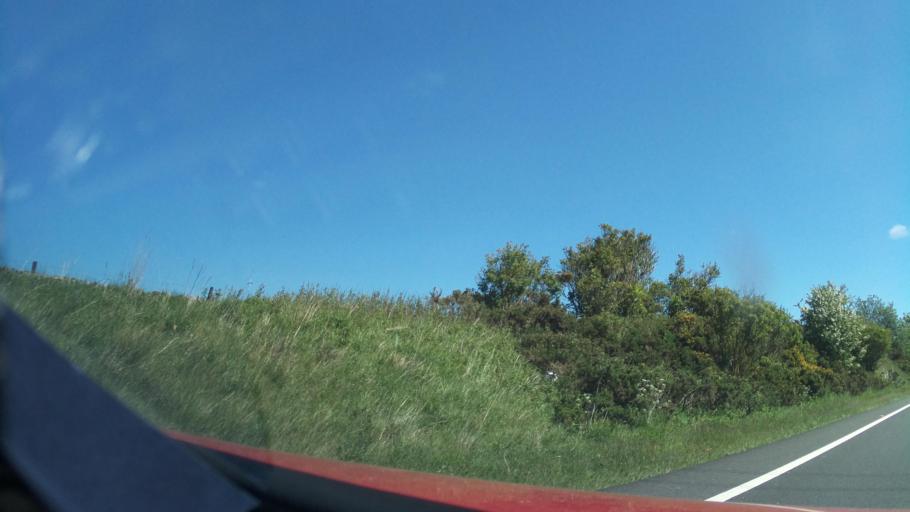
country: GB
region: Scotland
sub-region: The Scottish Borders
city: Hawick
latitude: 55.4733
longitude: -2.7998
